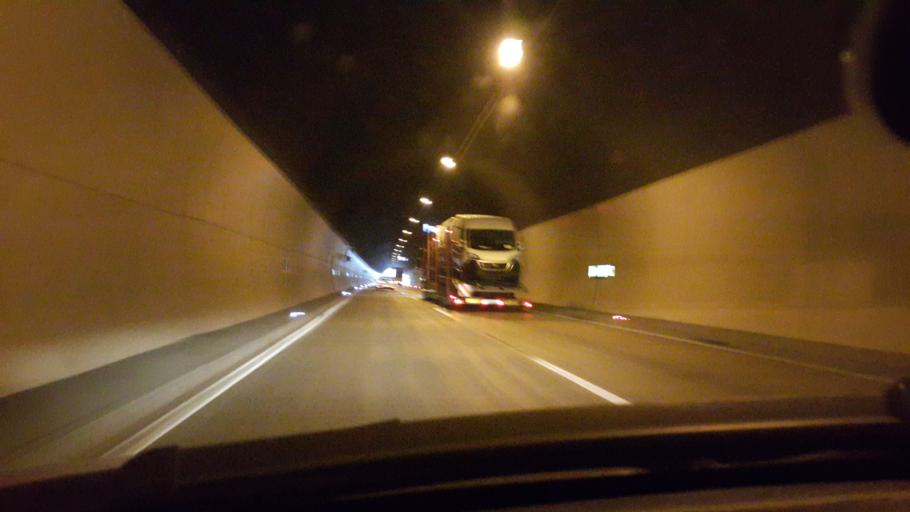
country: SI
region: Slovenska Konjice
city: Slovenske Konjice
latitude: 46.3141
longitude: 15.4581
